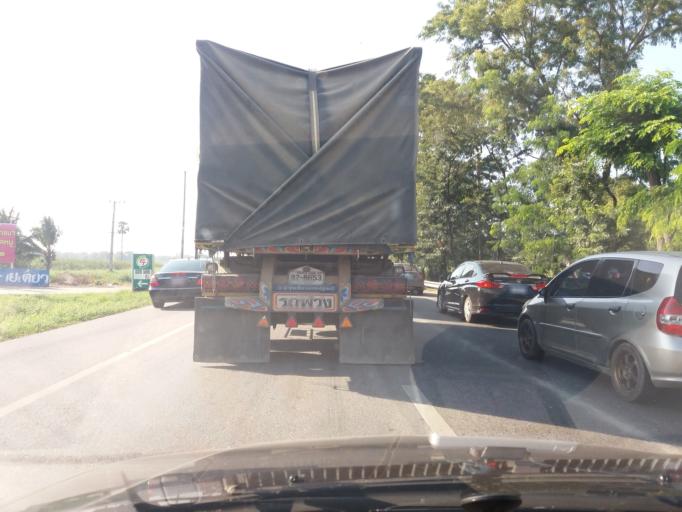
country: TH
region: Nakhon Sawan
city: Nakhon Sawan
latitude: 15.7348
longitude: 100.0258
